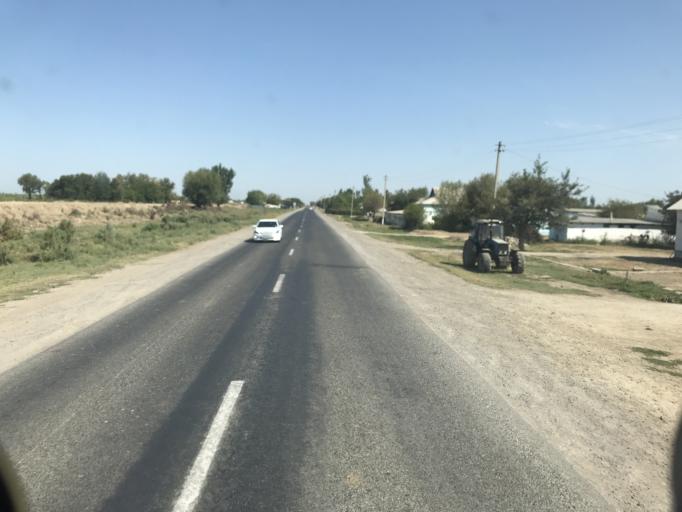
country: KZ
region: Ongtustik Qazaqstan
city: Myrzakent
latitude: 40.7571
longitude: 68.5370
